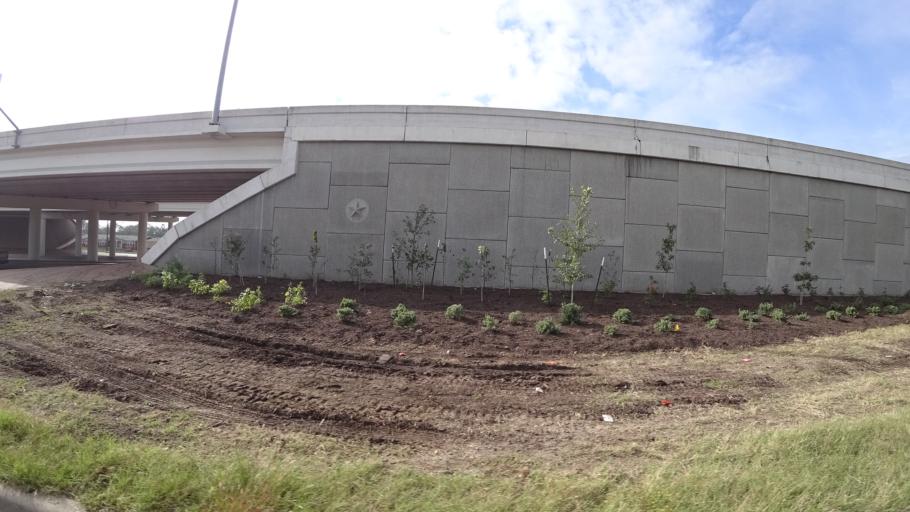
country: US
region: Texas
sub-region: Travis County
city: Austin
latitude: 30.2127
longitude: -97.7127
